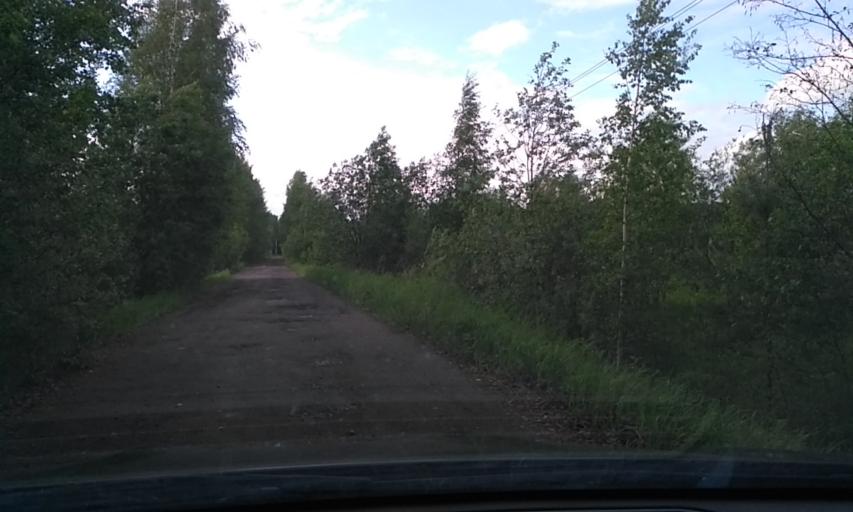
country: RU
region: Leningrad
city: Otradnoye
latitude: 59.8118
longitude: 30.8267
